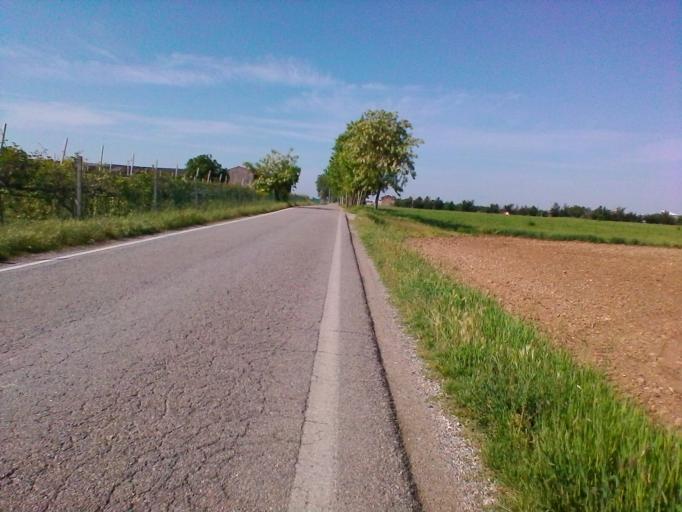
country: IT
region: Lombardy
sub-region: Provincia di Mantova
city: Malavicina
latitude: 45.2966
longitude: 10.7522
